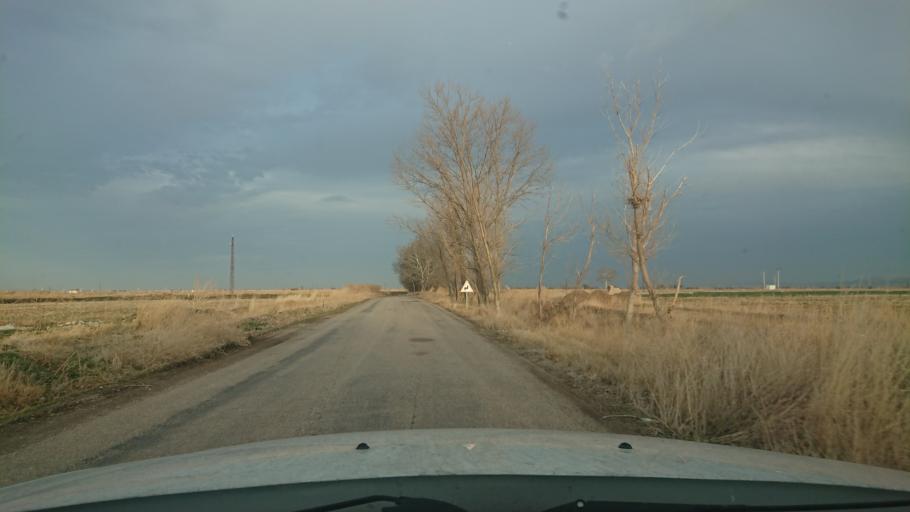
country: TR
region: Aksaray
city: Yesilova
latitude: 38.4468
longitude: 33.8362
